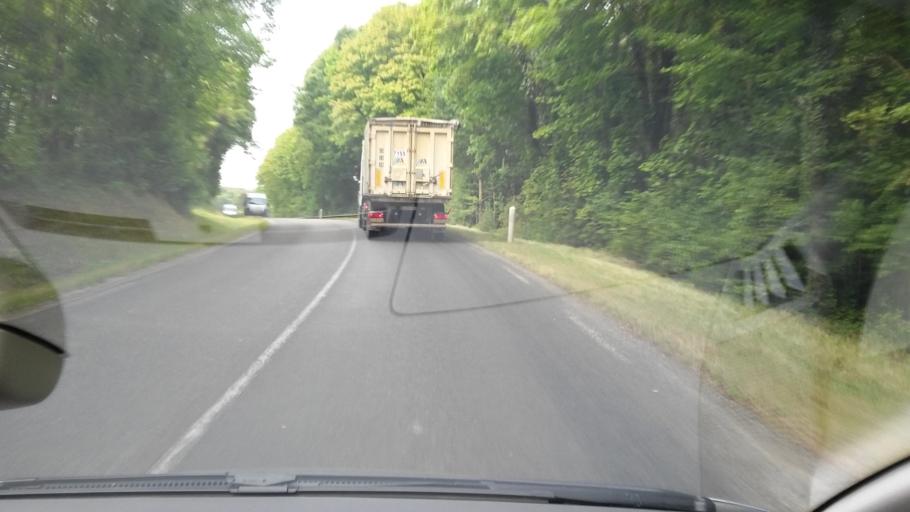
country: FR
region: Champagne-Ardenne
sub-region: Departement de la Marne
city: Tours-sur-Marne
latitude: 49.1061
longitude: 4.1150
